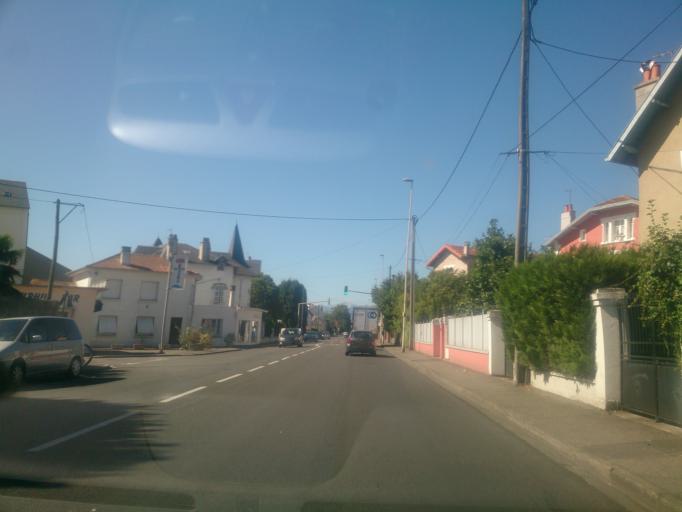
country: FR
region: Midi-Pyrenees
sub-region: Departement des Hautes-Pyrenees
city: Tarbes
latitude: 43.2252
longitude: 0.0661
